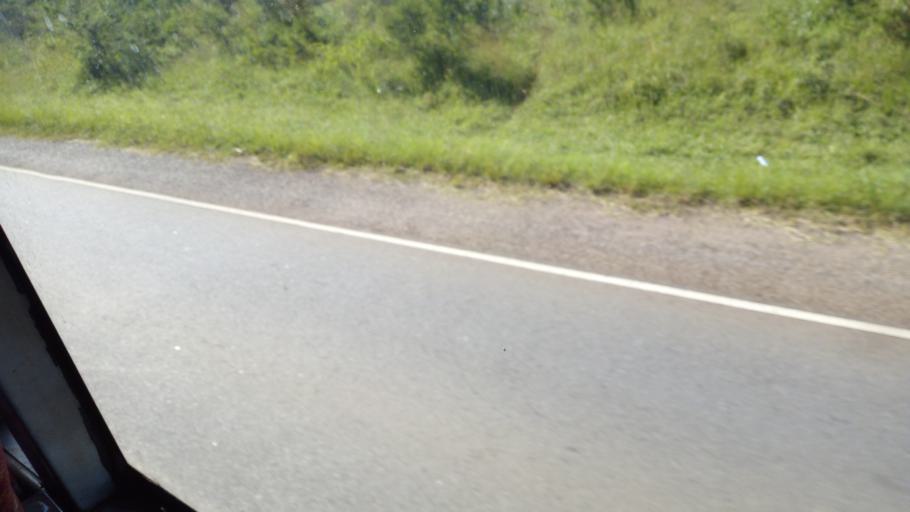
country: UG
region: Central Region
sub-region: Lyantonde District
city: Lyantonde
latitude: -0.4540
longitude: 31.0531
